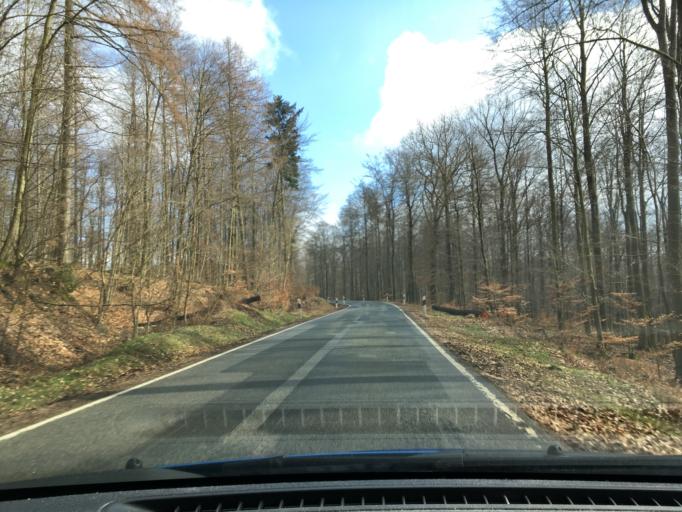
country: DE
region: Lower Saxony
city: Buhren
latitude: 51.5000
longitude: 9.6426
